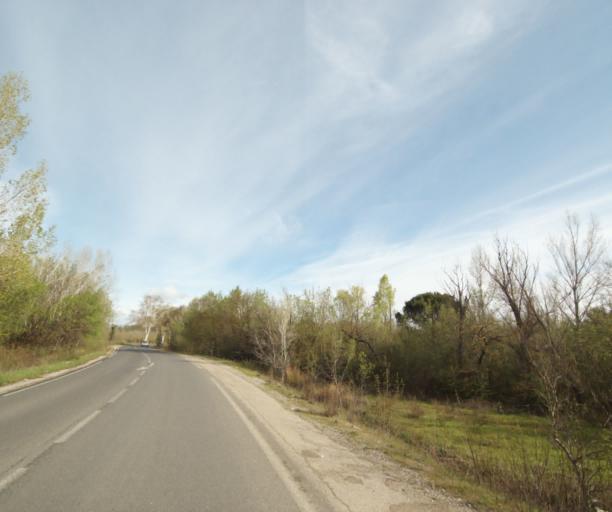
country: FR
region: Languedoc-Roussillon
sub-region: Departement de l'Herault
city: Saint-Jean-de-Vedas
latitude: 43.5843
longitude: 3.8194
